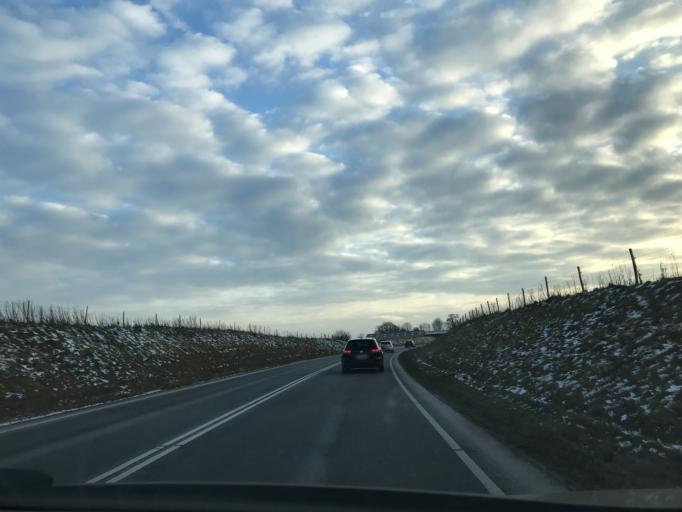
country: DK
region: Capital Region
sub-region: Egedal Kommune
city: Smorumnedre
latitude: 55.7234
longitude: 12.3152
